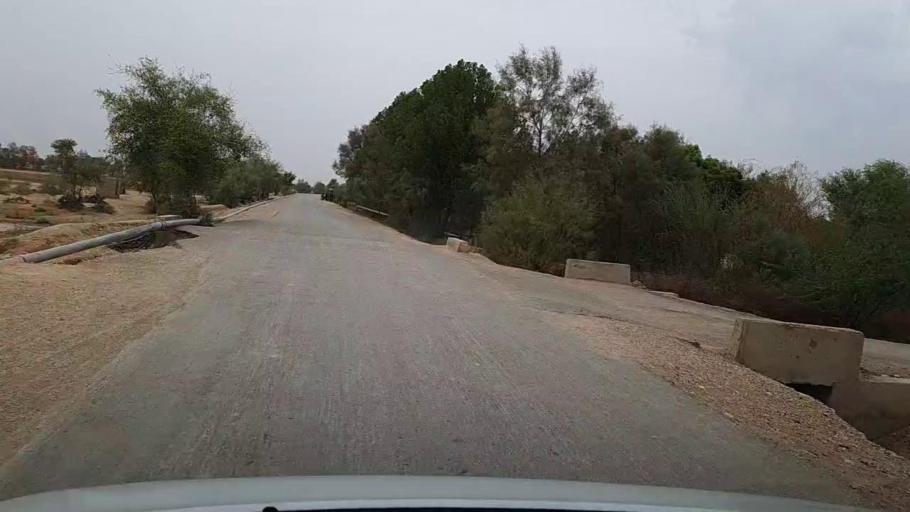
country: PK
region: Sindh
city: Sehwan
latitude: 26.3217
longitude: 67.7307
